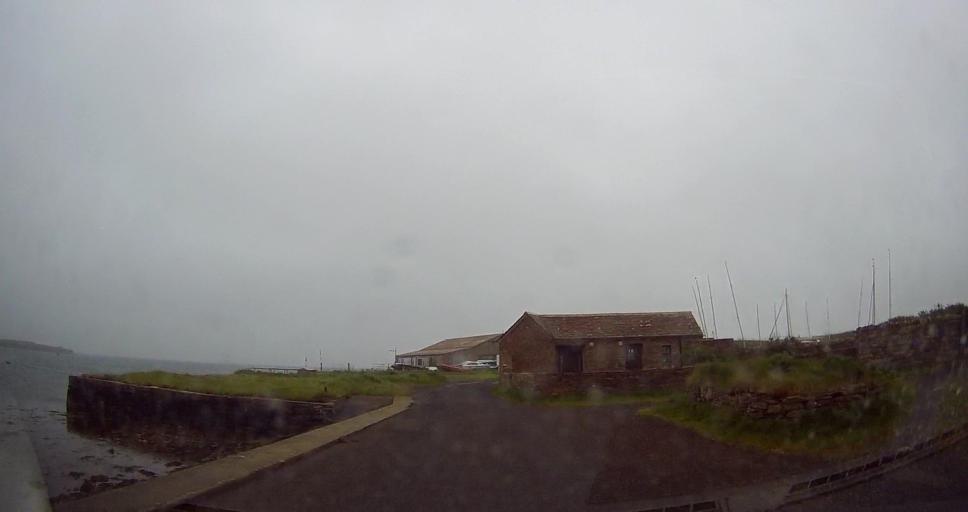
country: GB
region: Scotland
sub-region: Orkney Islands
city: Stromness
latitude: 58.9536
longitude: -3.2987
